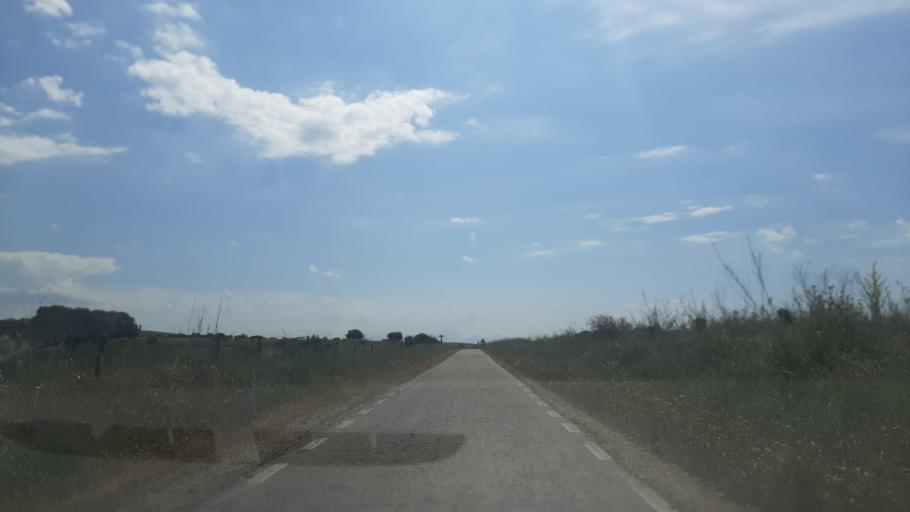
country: ES
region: Castille and Leon
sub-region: Provincia de Salamanca
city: Aldea del Obispo
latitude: 40.6531
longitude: -6.7692
